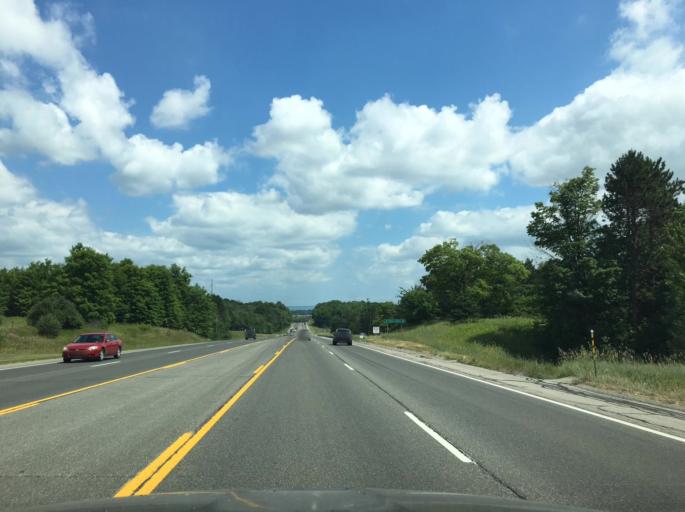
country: US
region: Michigan
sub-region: Grand Traverse County
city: Traverse City
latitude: 44.7048
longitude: -85.6538
